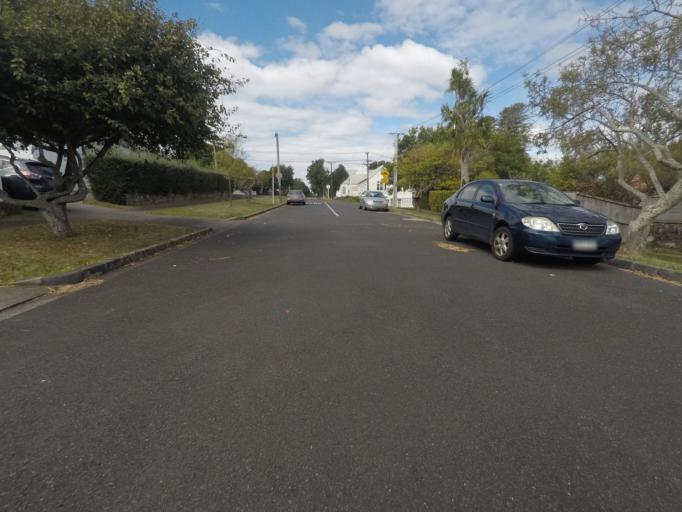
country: NZ
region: Auckland
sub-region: Auckland
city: Rosebank
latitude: -36.8810
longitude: 174.7183
